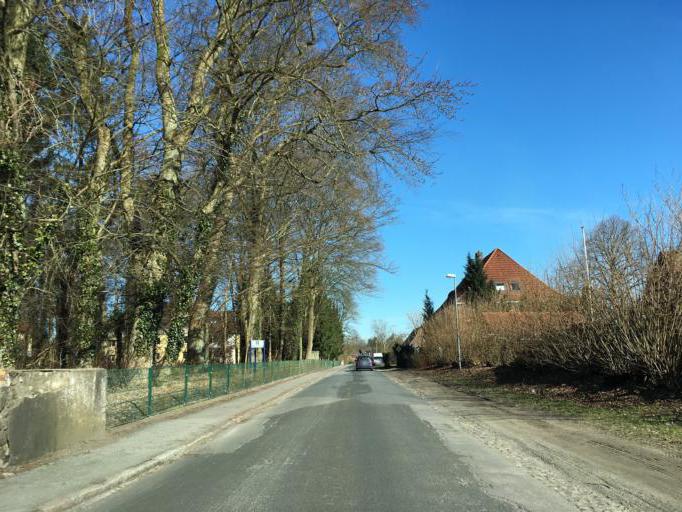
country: DE
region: Schleswig-Holstein
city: Lehmrade
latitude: 53.5908
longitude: 10.7532
